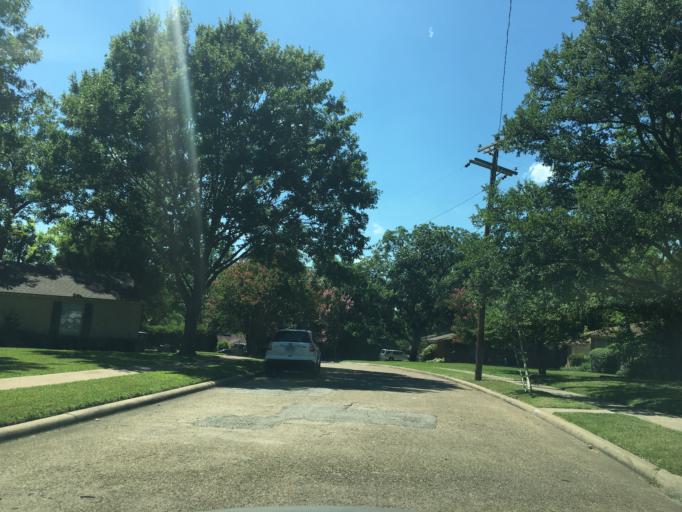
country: US
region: Texas
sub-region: Dallas County
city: Highland Park
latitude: 32.8387
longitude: -96.7014
